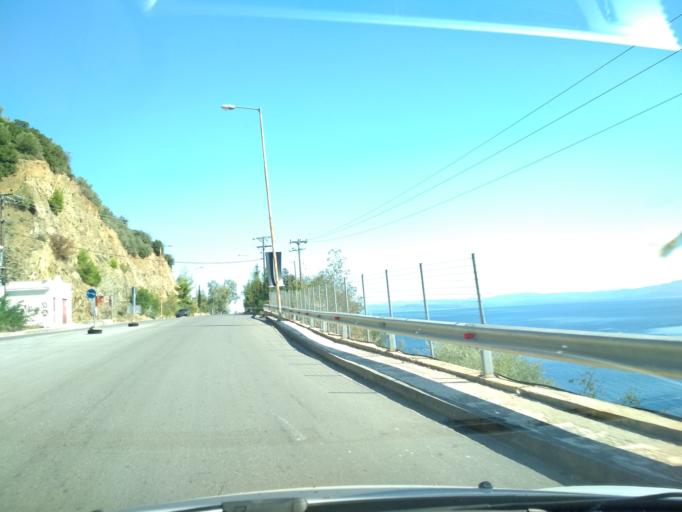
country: GR
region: Central Greece
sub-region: Nomos Evvoias
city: Oreoi
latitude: 38.8515
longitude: 23.0572
